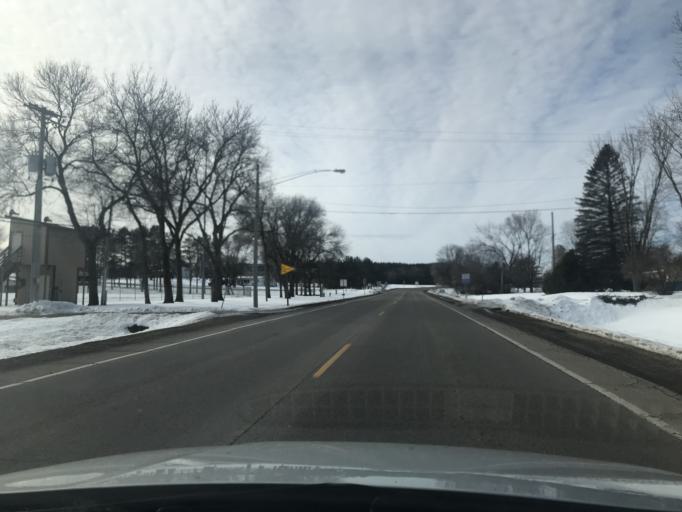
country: US
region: Wisconsin
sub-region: Oconto County
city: Gillett
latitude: 44.8871
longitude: -88.3164
